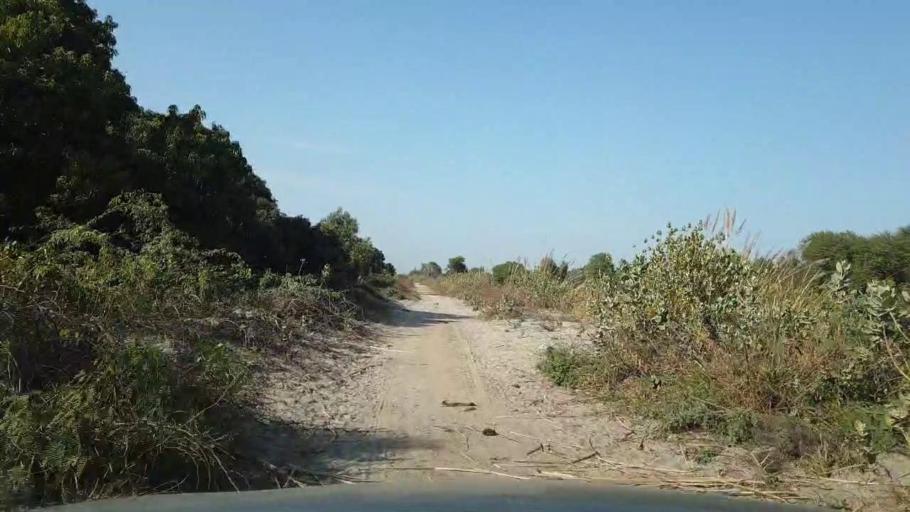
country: PK
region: Sindh
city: Tando Adam
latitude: 25.6064
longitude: 68.6240
